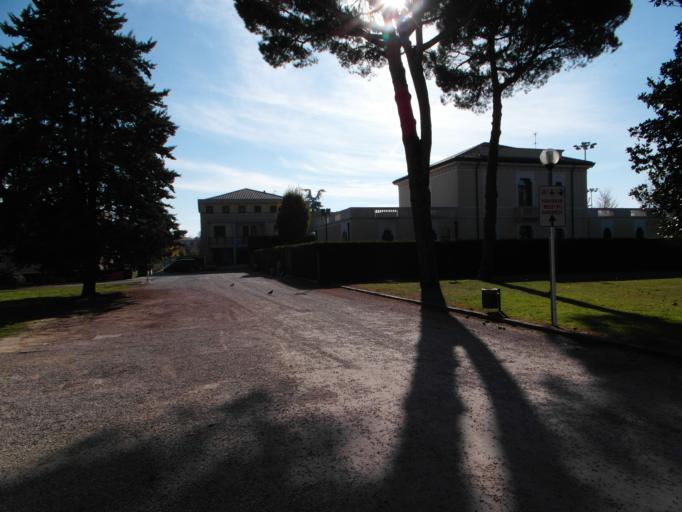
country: IT
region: Veneto
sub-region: Provincia di Padova
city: Piazzola sul Brenta
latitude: 45.5426
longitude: 11.7818
